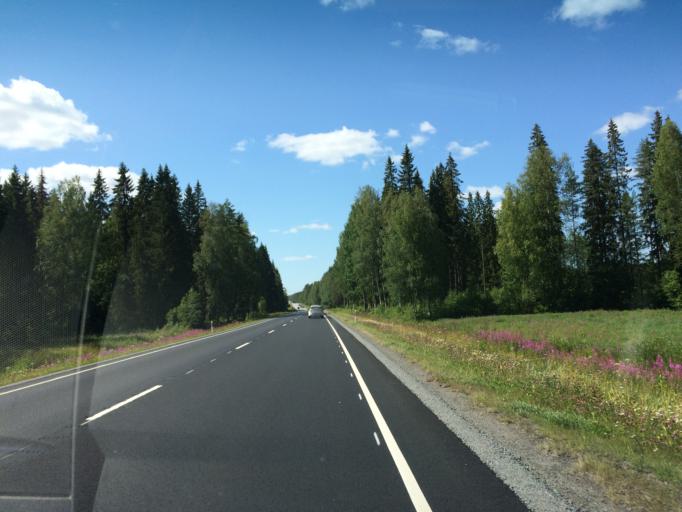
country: FI
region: Pirkanmaa
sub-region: Lounais-Pirkanmaa
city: Kiikoinen
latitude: 61.4758
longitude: 22.4571
